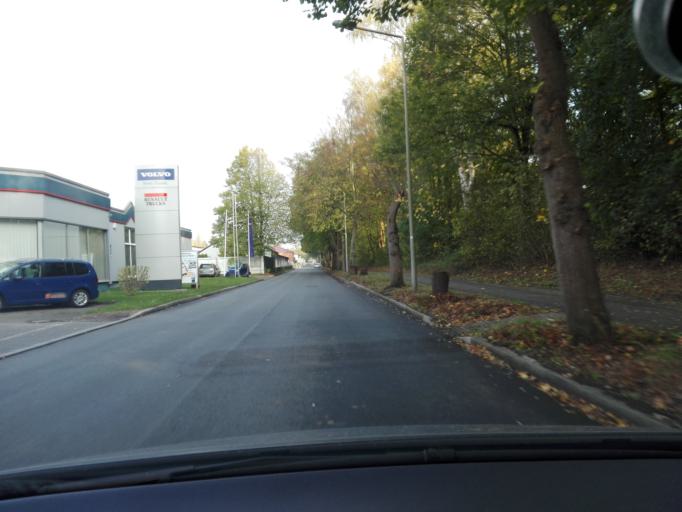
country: DE
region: North Rhine-Westphalia
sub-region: Regierungsbezirk Arnsberg
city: Unna
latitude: 51.5533
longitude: 7.6913
